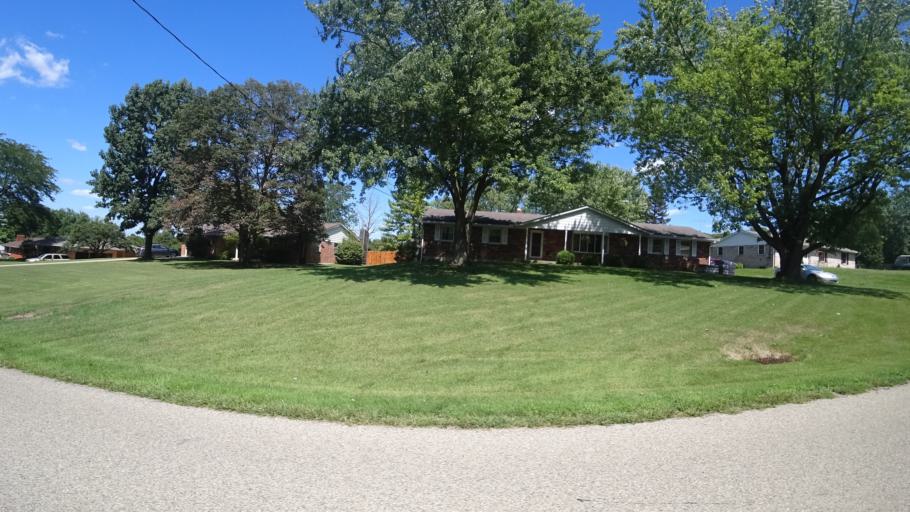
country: US
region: Ohio
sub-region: Butler County
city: New Miami
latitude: 39.4119
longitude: -84.5243
